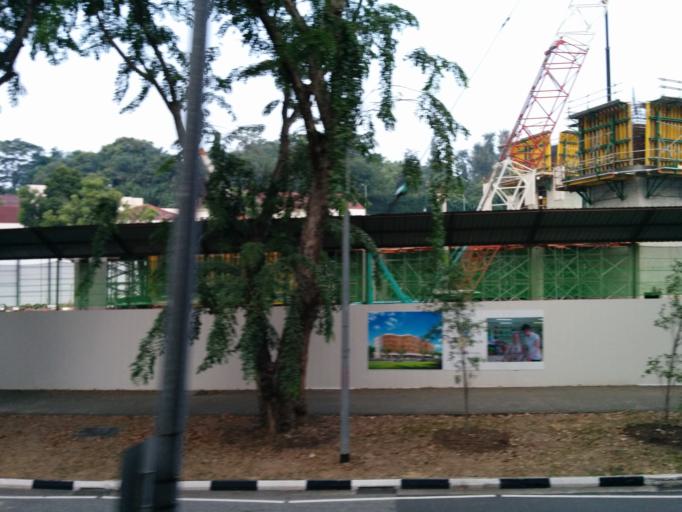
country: SG
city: Singapore
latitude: 1.2708
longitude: 103.8117
